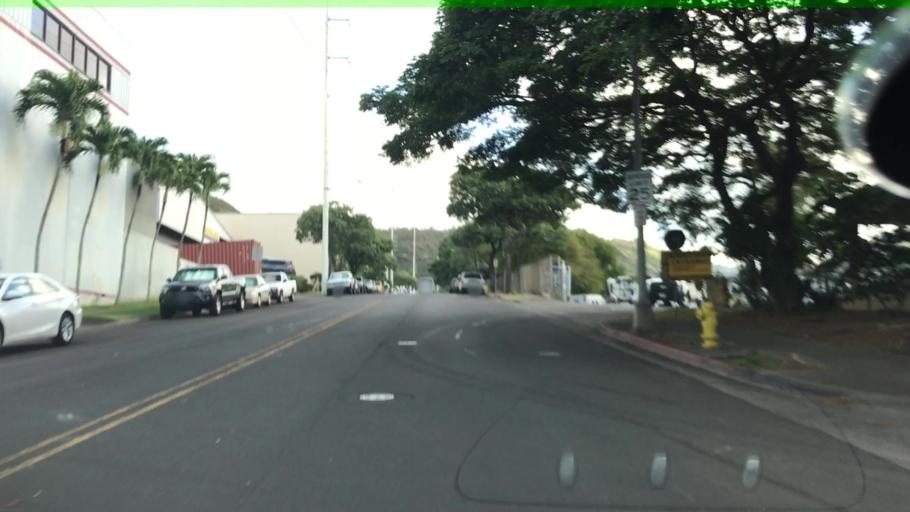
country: US
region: Hawaii
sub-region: Honolulu County
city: Halawa Heights
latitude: 21.3755
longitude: -157.9112
